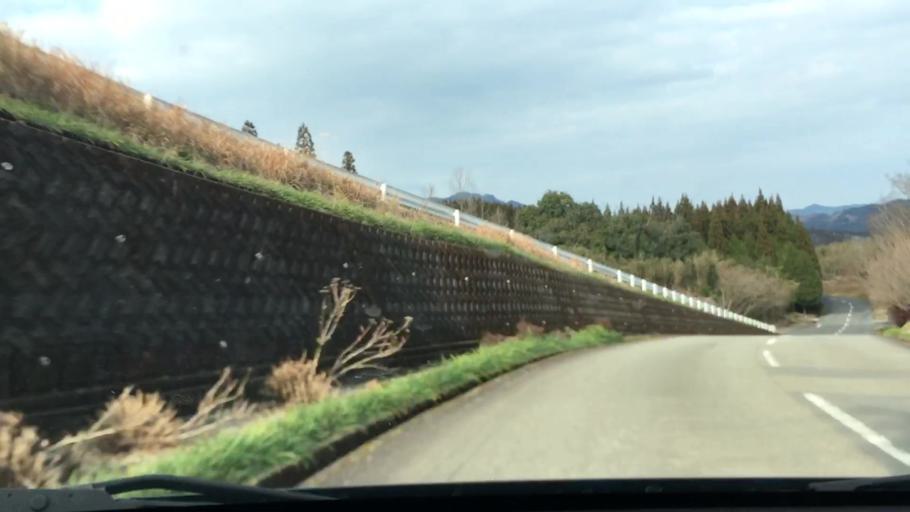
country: JP
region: Miyazaki
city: Nichinan
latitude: 31.6180
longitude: 131.3354
